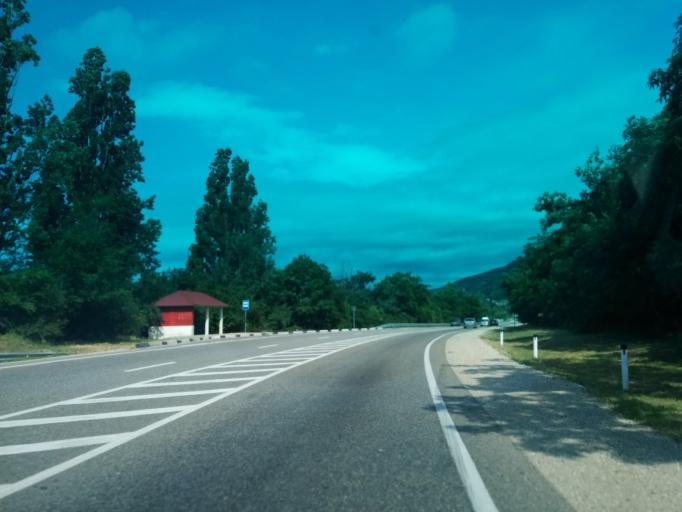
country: RU
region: Krasnodarskiy
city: Nebug
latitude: 44.1553
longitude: 39.0061
